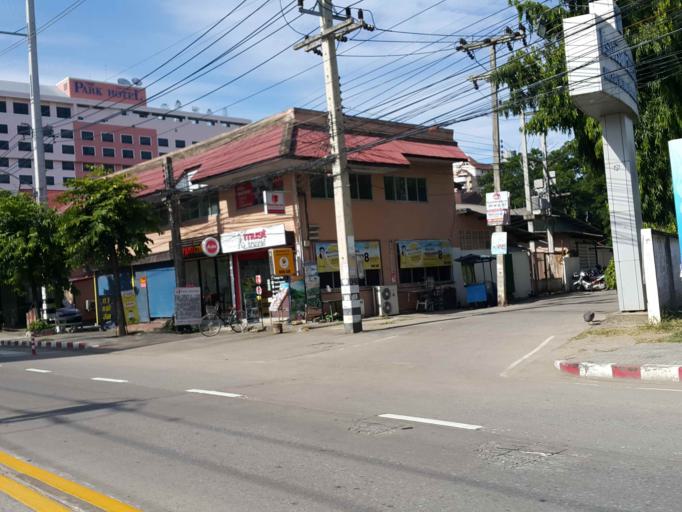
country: TH
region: Chiang Mai
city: Chiang Mai
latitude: 18.7681
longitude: 98.9993
